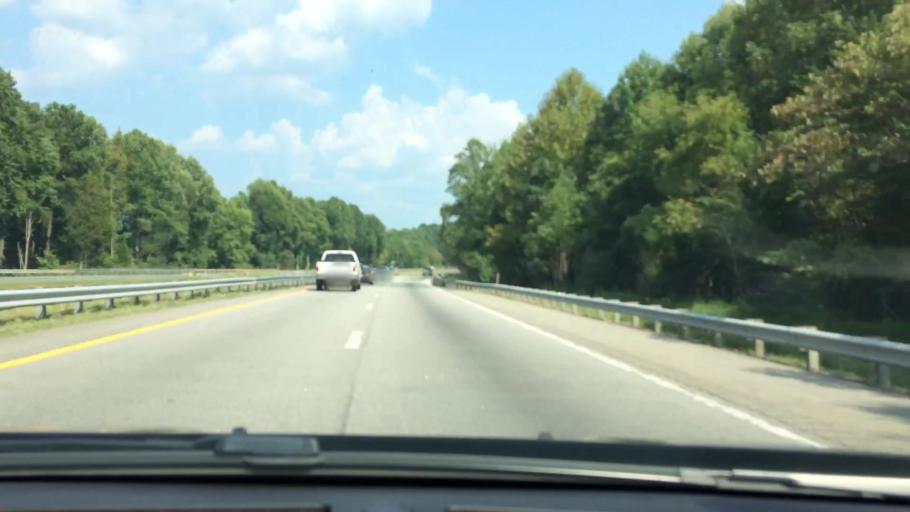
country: US
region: North Carolina
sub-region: Orange County
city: Hillsborough
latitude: 36.0591
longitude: -79.1137
